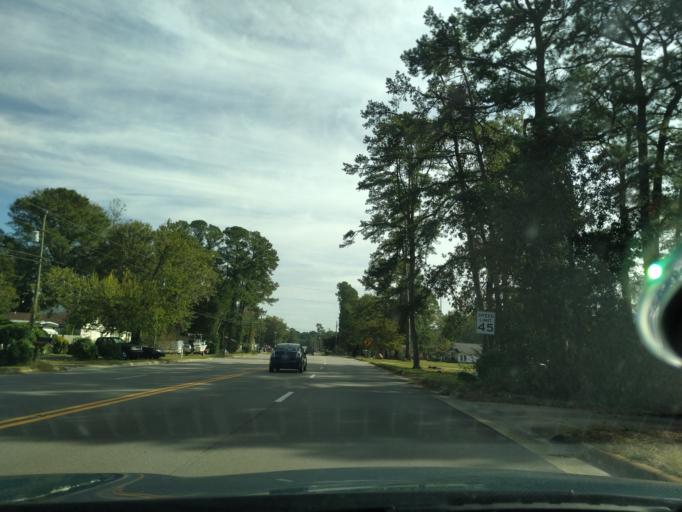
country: US
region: North Carolina
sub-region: Beaufort County
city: River Road
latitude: 35.5236
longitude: -77.0094
